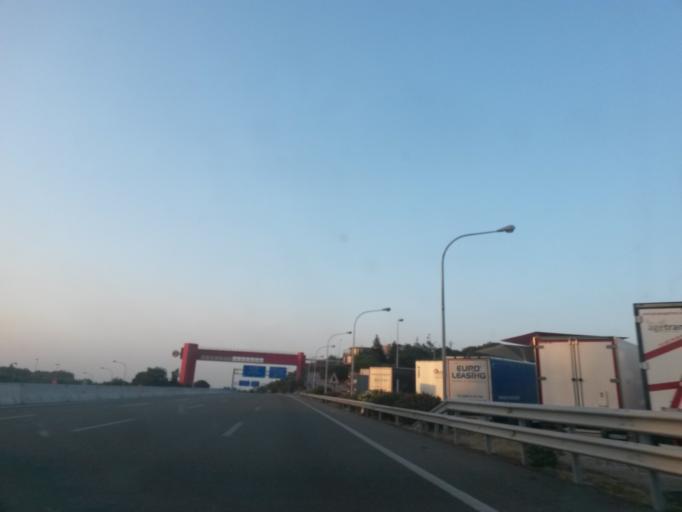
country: ES
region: Catalonia
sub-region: Provincia de Girona
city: Macanet de la Selva
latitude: 41.7719
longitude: 2.7389
